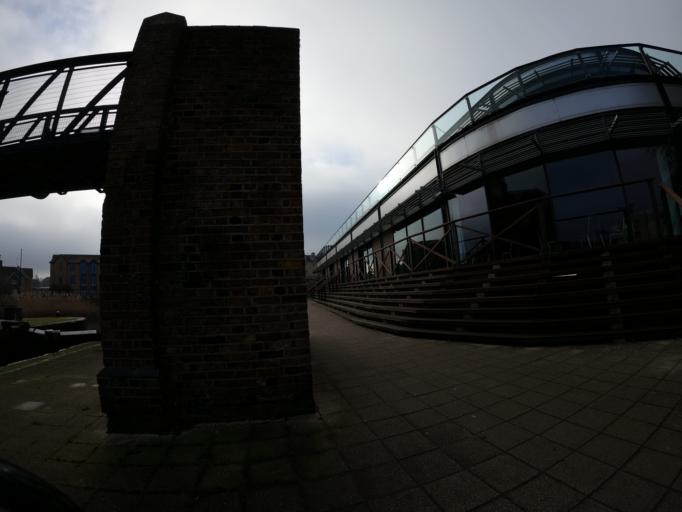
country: GB
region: England
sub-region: Greater London
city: Brentford
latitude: 51.4831
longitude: -0.3119
